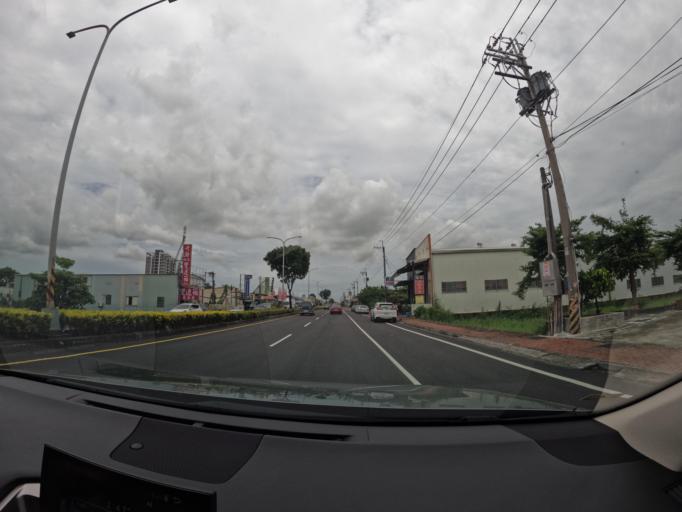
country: TW
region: Taiwan
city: Fengshan
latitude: 22.7857
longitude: 120.3094
